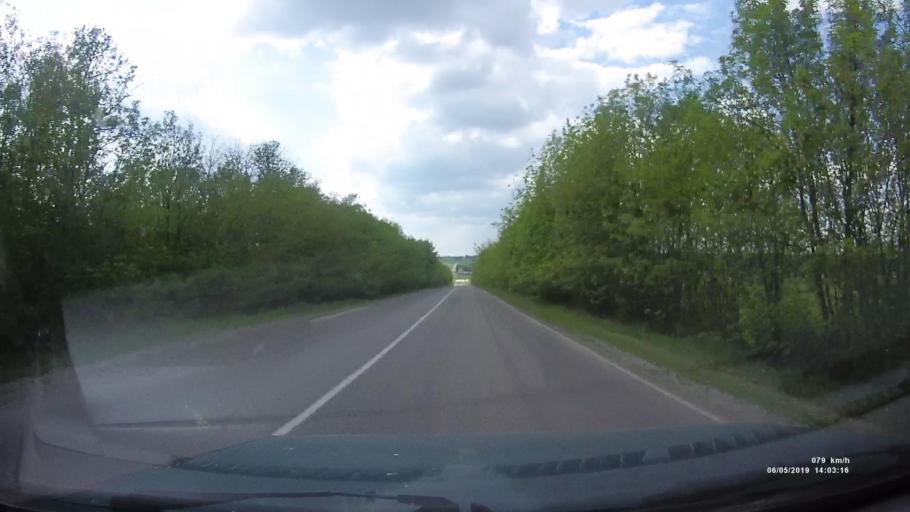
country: RU
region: Rostov
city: Shakhty
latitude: 47.6813
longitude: 40.3492
